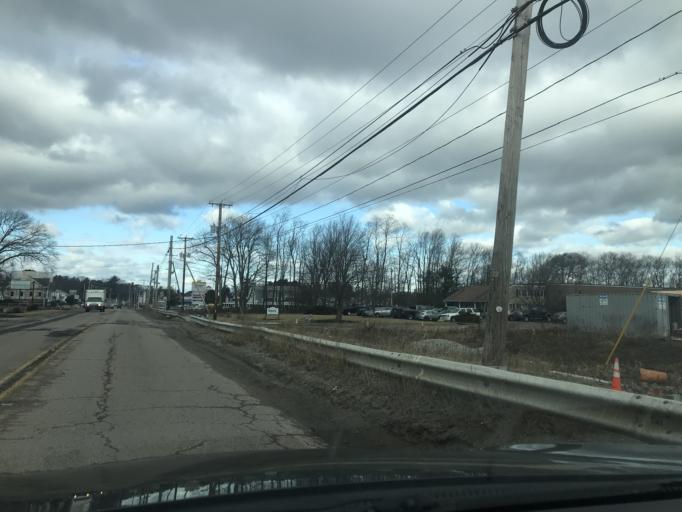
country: US
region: Massachusetts
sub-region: Plymouth County
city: Rockland
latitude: 42.1436
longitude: -70.9536
